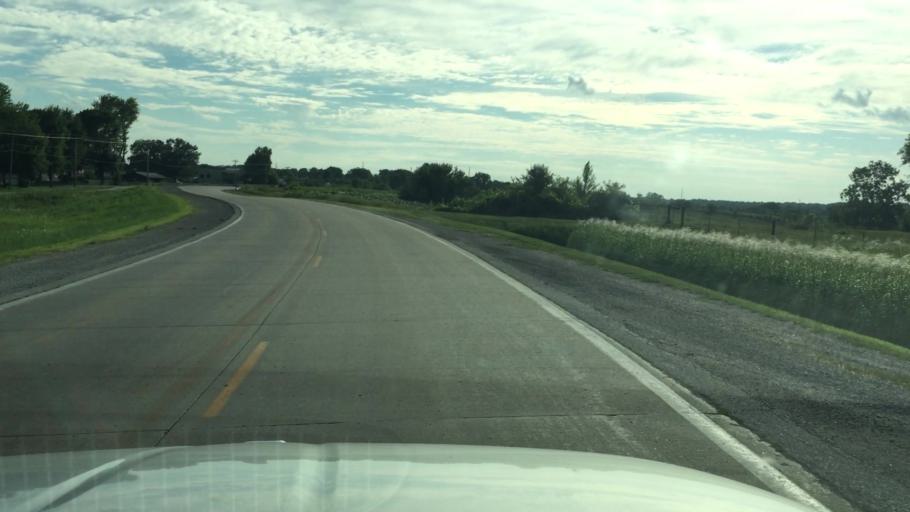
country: US
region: Iowa
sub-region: Johnson County
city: Iowa City
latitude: 41.6710
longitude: -91.4752
